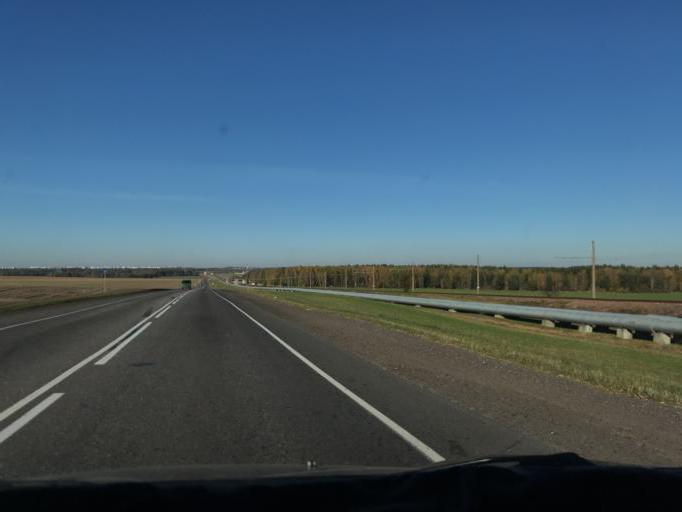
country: BY
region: Gomel
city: Mazyr
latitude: 51.9729
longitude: 29.2609
